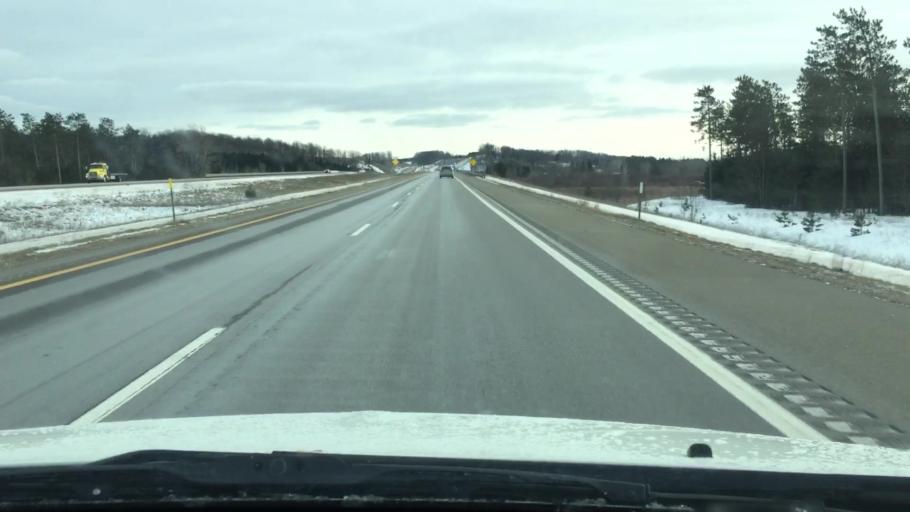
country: US
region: Michigan
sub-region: Wexford County
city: Manton
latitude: 44.4320
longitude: -85.3910
